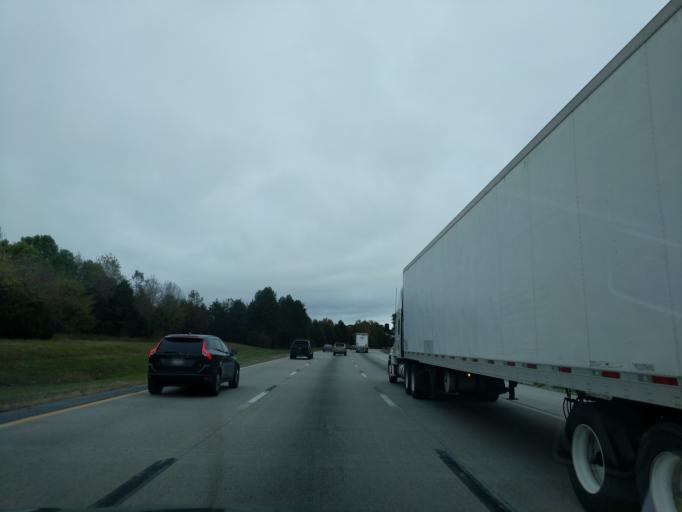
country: US
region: North Carolina
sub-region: Guilford County
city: Jamestown
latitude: 35.9792
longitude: -79.8884
